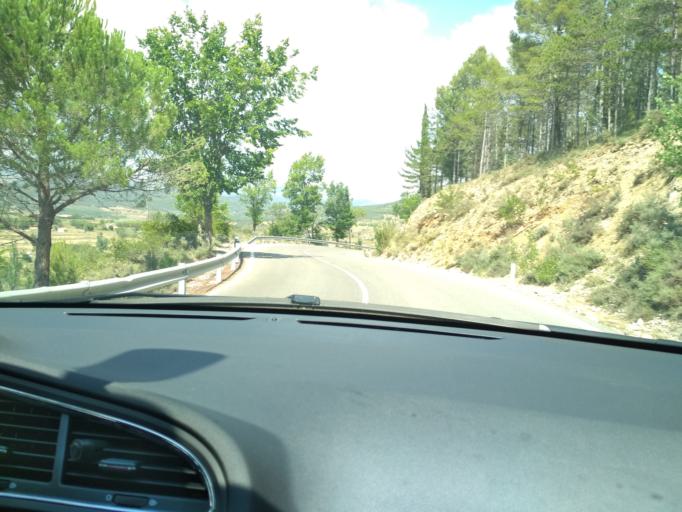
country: ES
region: Aragon
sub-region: Provincia de Teruel
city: Rubielos de Mora
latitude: 40.1889
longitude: -0.6490
